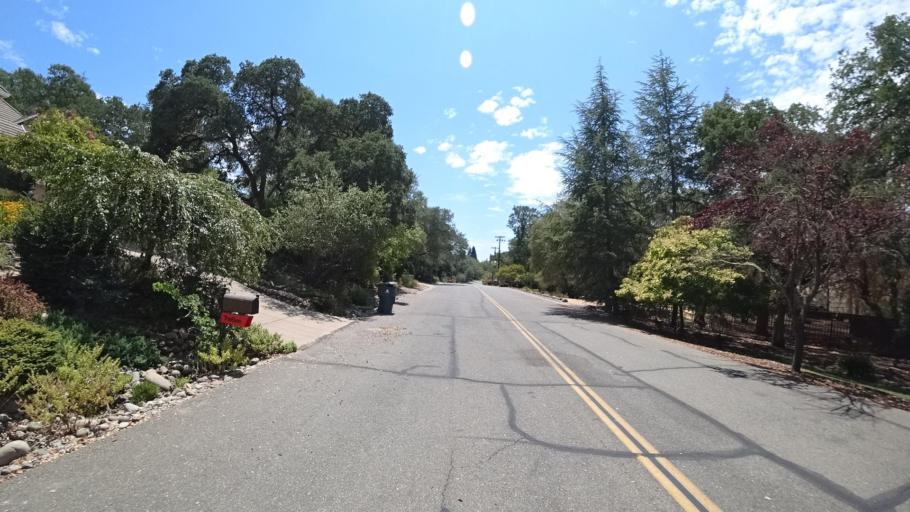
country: US
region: California
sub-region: Placer County
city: Rocklin
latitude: 38.8188
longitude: -121.2316
